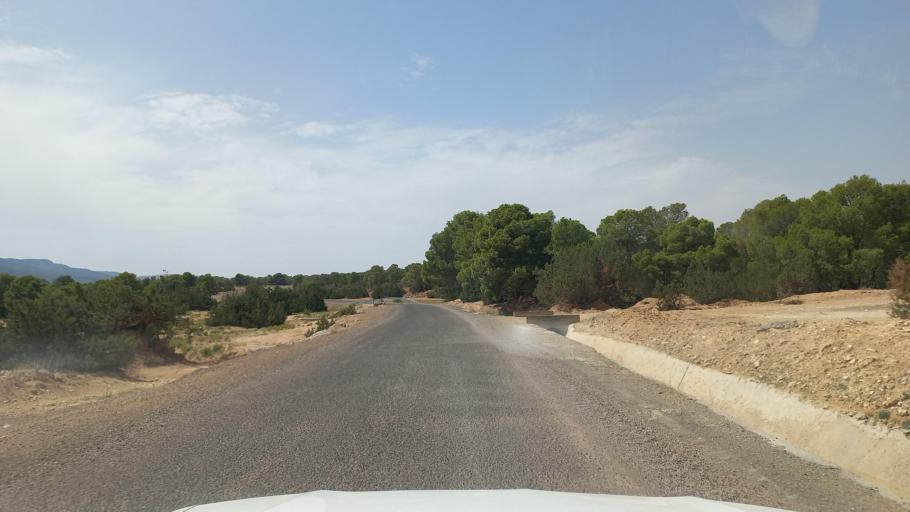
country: TN
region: Al Qasrayn
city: Sbiba
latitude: 35.3860
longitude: 8.9420
